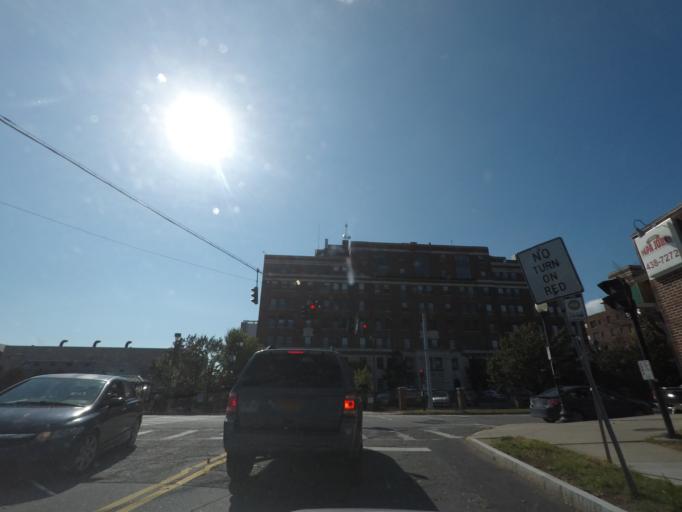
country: US
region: New York
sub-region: Albany County
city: West Albany
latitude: 42.6569
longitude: -73.8023
